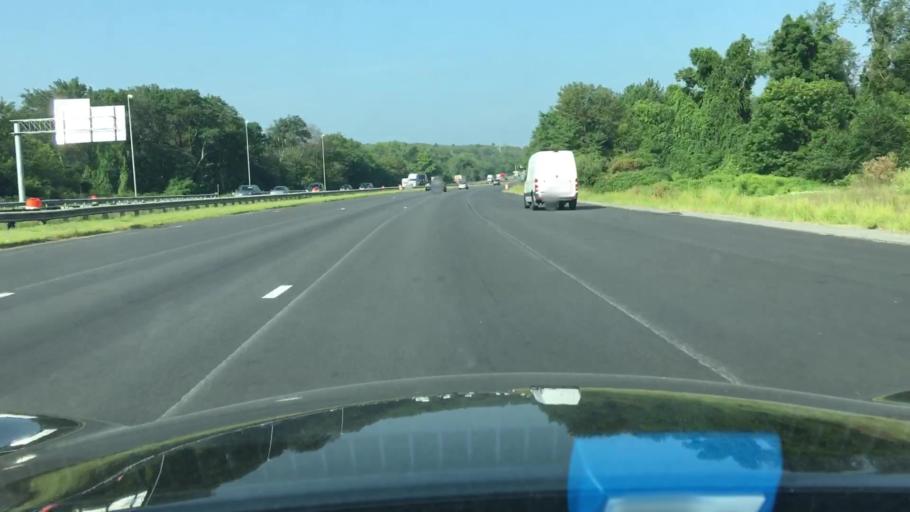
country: US
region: Massachusetts
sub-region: Worcester County
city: Millbury
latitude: 42.2058
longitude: -71.7895
